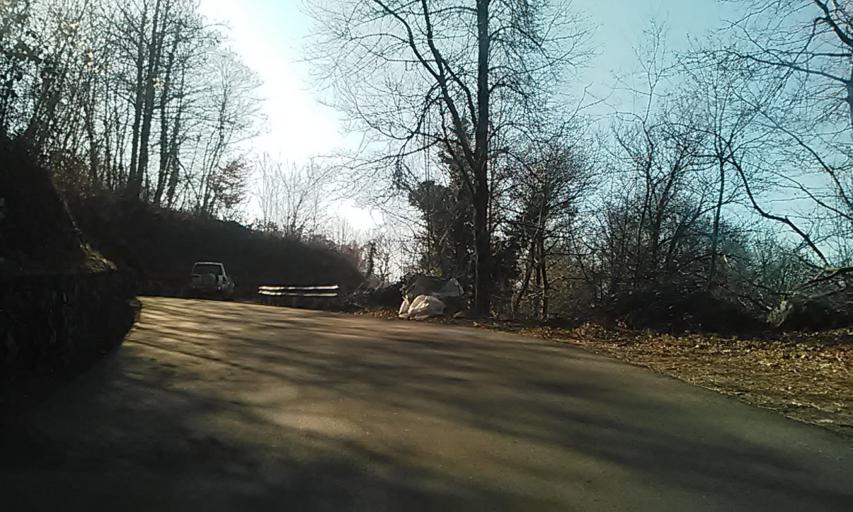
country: IT
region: Piedmont
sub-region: Provincia di Vercelli
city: Quarona
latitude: 45.7608
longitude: 8.2783
